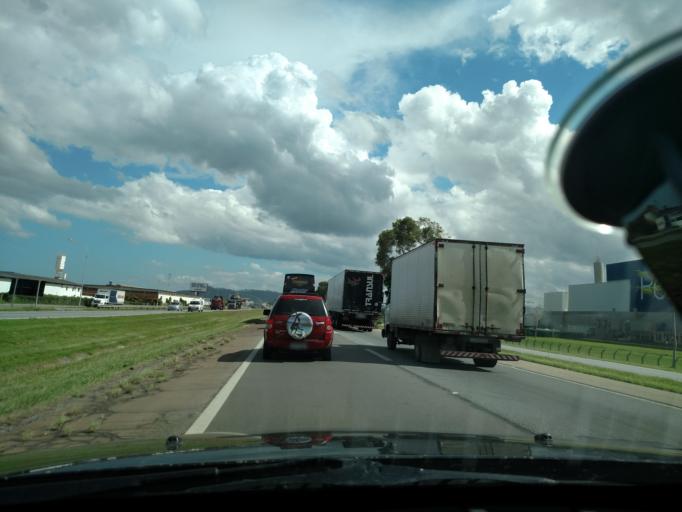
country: BR
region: Santa Catarina
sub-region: Tijucas
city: Tijucas
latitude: -27.2251
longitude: -48.6277
